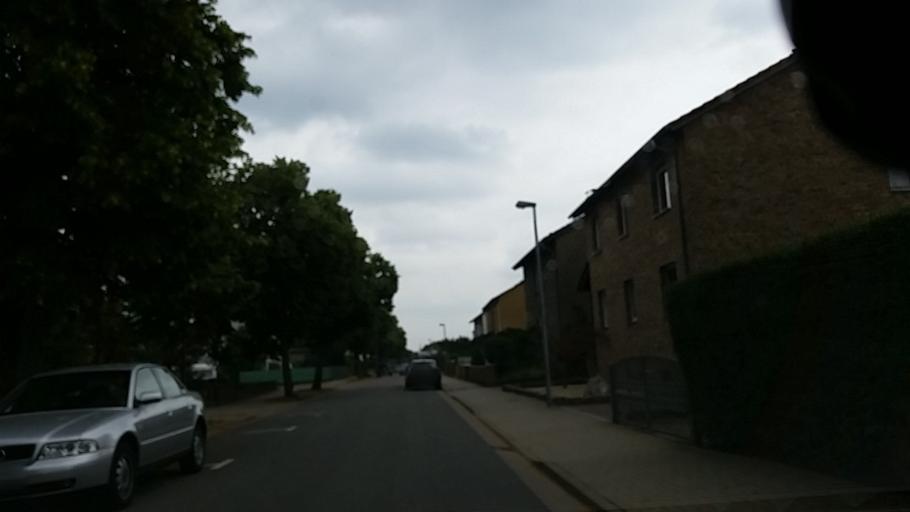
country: DE
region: Lower Saxony
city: Danndorf
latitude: 52.4321
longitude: 10.8531
